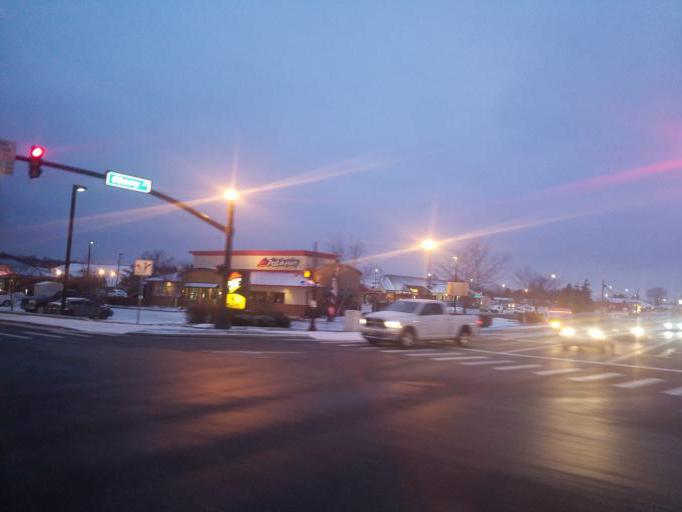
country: US
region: Ohio
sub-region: Delaware County
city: Sunbury
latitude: 40.2480
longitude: -82.8682
